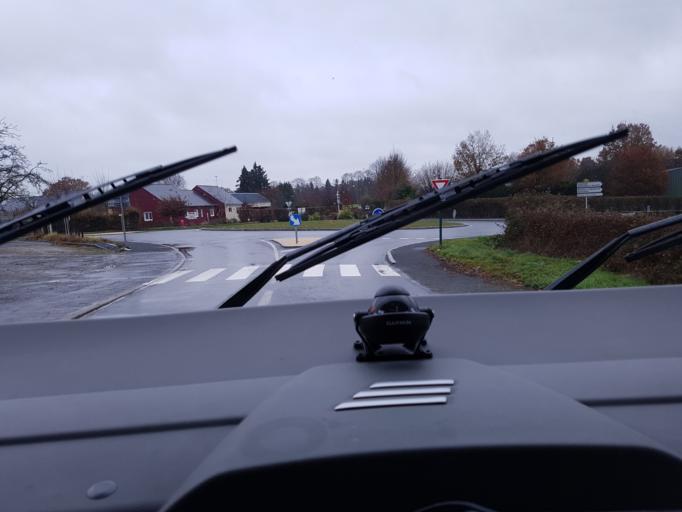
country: FR
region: Pays de la Loire
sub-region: Departement de la Mayenne
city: Gorron
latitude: 48.4154
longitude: -0.8242
